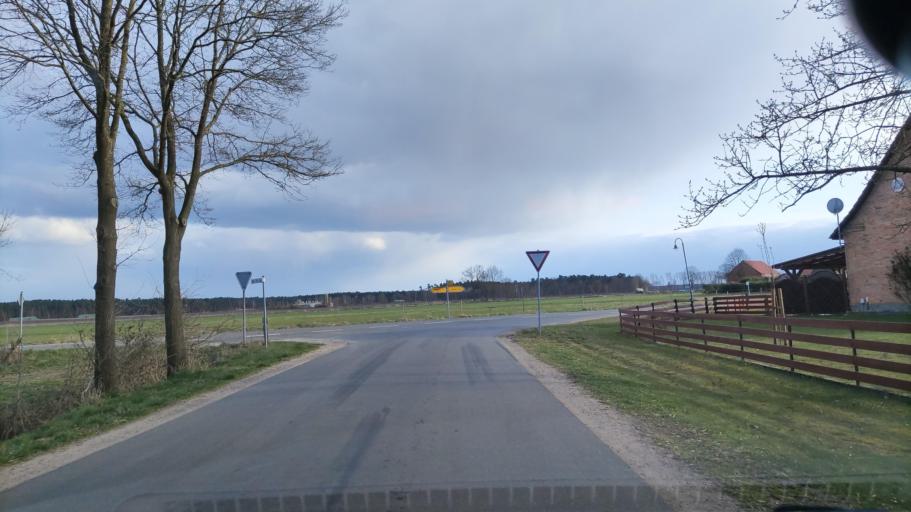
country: DE
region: Lower Saxony
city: Trebel
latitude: 53.0288
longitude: 11.2690
